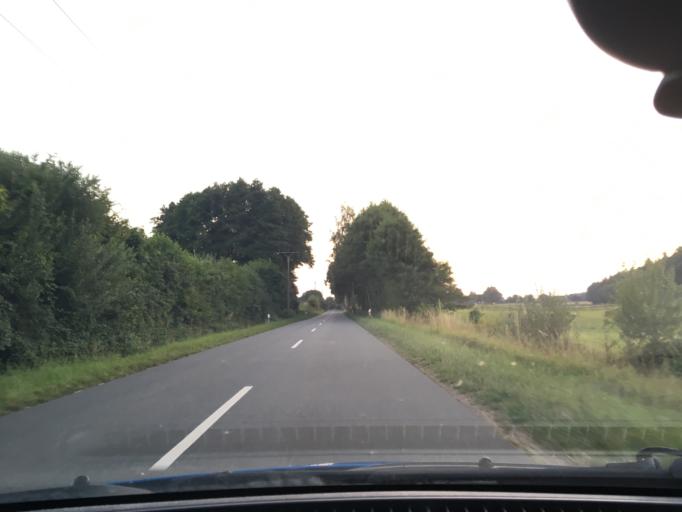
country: DE
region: Lower Saxony
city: Natendorf
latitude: 53.0972
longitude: 10.4342
